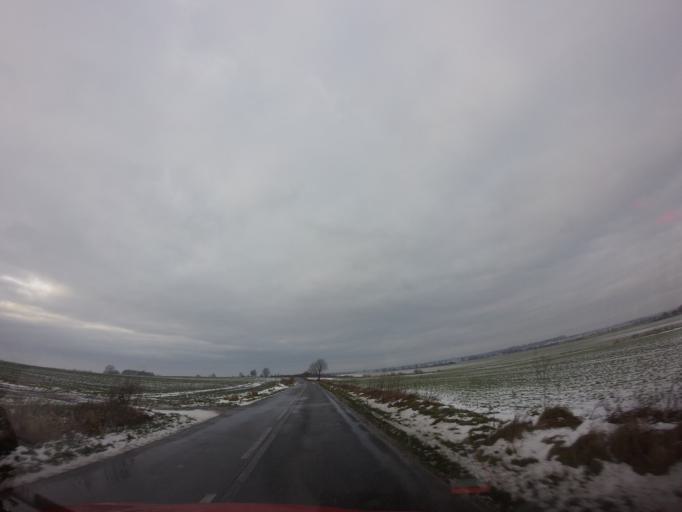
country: PL
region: West Pomeranian Voivodeship
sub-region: Powiat choszczenski
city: Pelczyce
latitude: 53.0580
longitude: 15.3594
